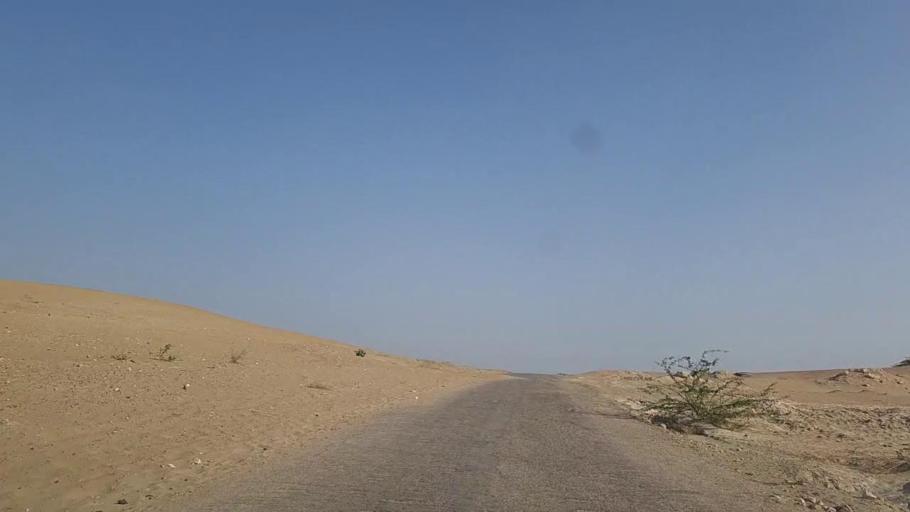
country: PK
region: Sindh
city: Naukot
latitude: 24.6287
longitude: 69.3636
